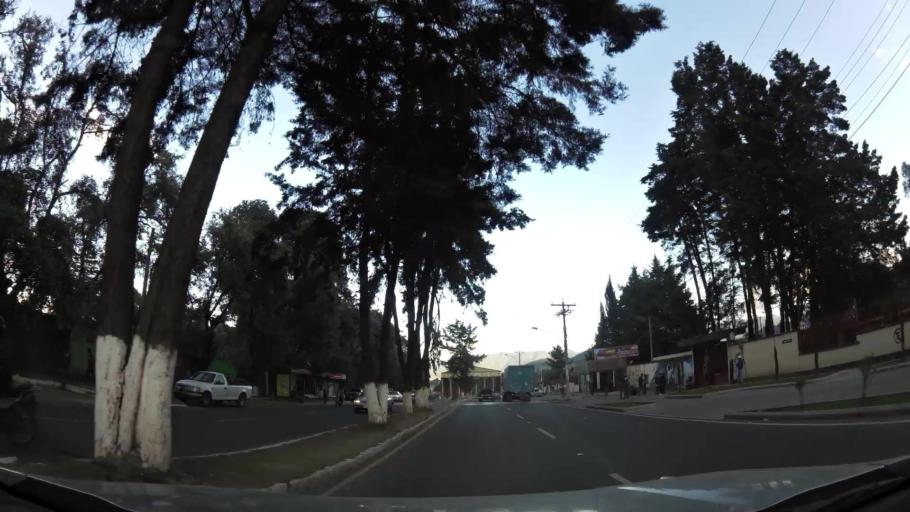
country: GT
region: Quetzaltenango
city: Quetzaltenango
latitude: 14.8463
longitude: -91.5357
